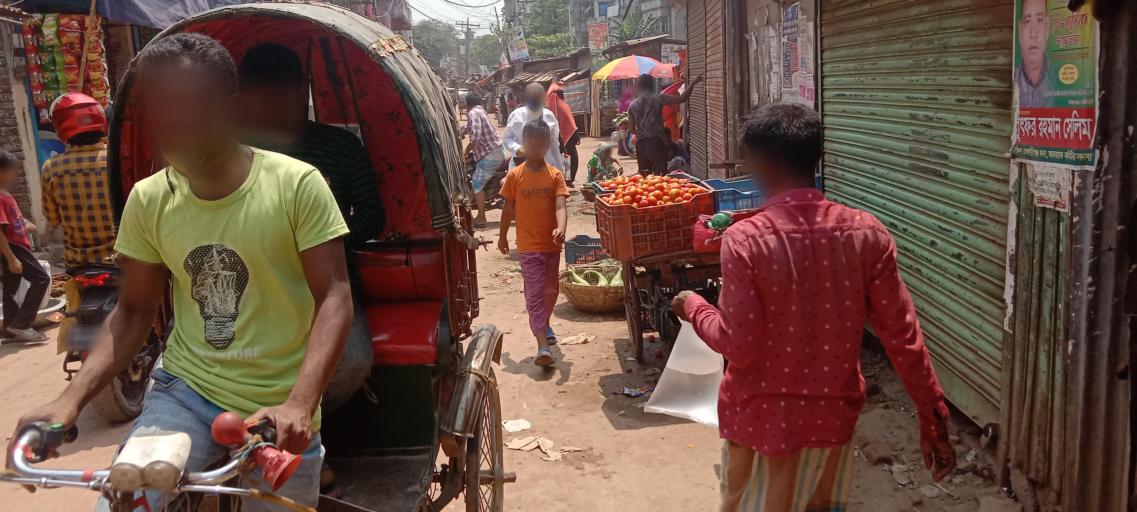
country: BD
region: Dhaka
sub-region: Dhaka
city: Dhaka
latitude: 23.6818
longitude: 90.4198
